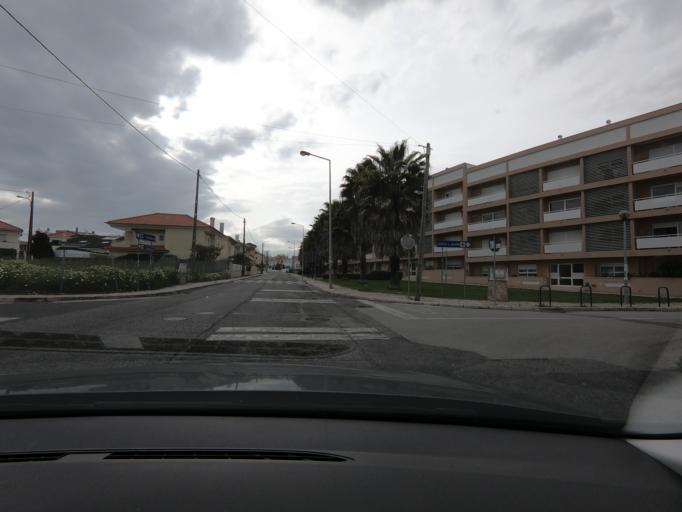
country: PT
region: Lisbon
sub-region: Cascais
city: Sao Domingos de Rana
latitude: 38.7123
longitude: -9.3356
